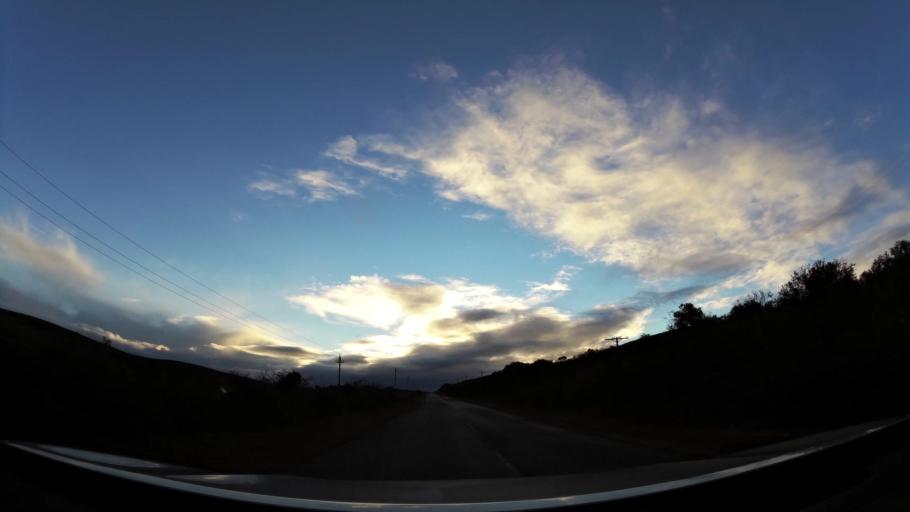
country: ZA
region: Western Cape
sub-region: Eden District Municipality
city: Riversdale
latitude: -34.0578
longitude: 20.8687
